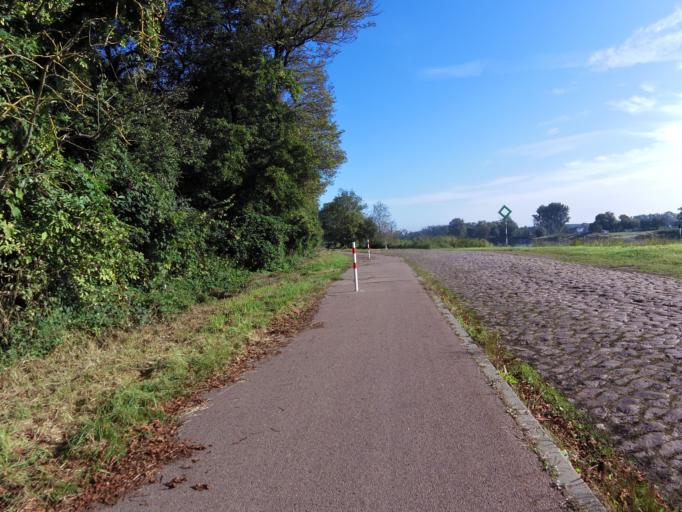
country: DE
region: Saxony-Anhalt
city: Coswig
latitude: 51.8716
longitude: 12.4471
